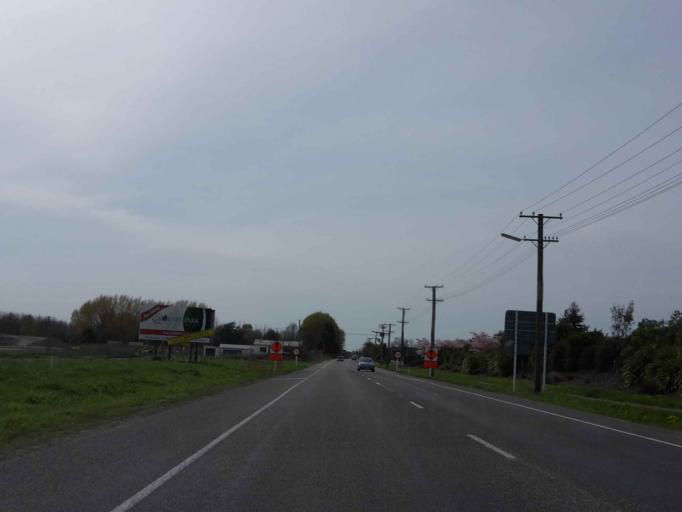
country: NZ
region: Canterbury
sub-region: Waimakariri District
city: Kaiapoi
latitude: -43.4523
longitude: 172.6139
